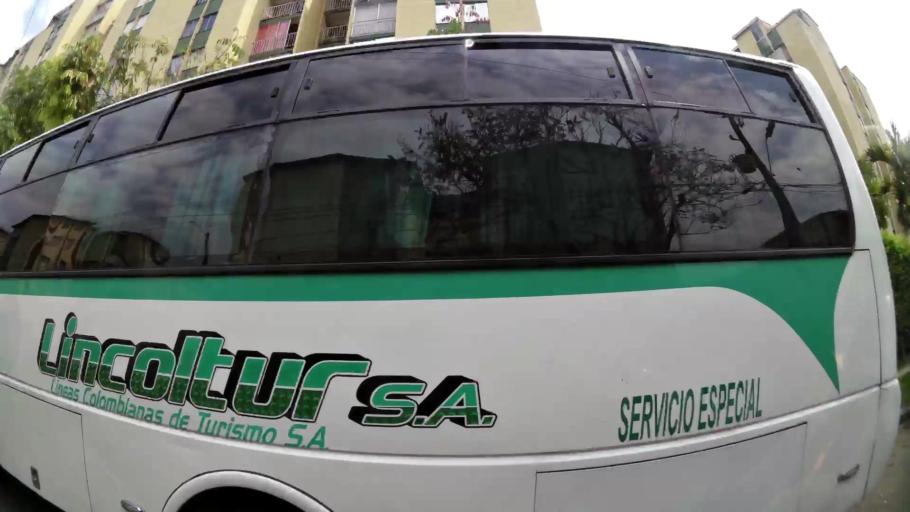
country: CO
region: Antioquia
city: Itagui
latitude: 6.1984
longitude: -75.5949
